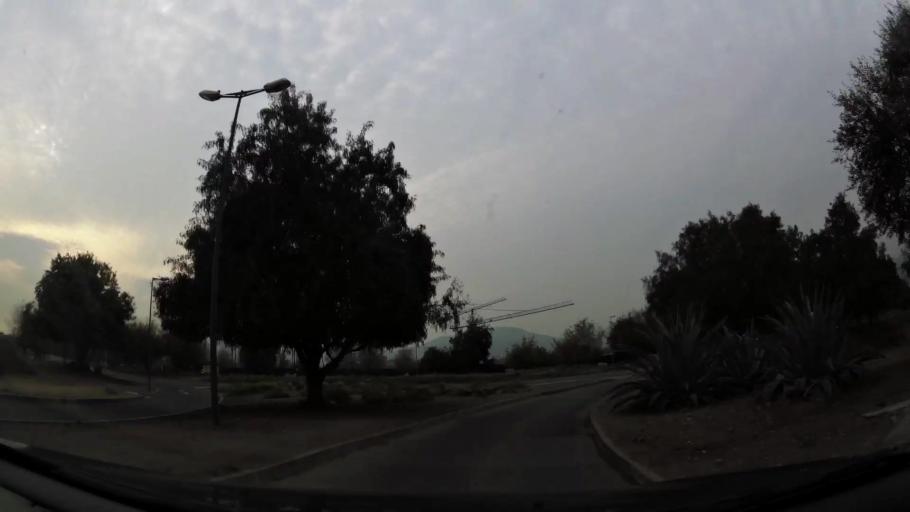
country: CL
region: Santiago Metropolitan
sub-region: Provincia de Chacabuco
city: Chicureo Abajo
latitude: -33.2804
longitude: -70.6273
